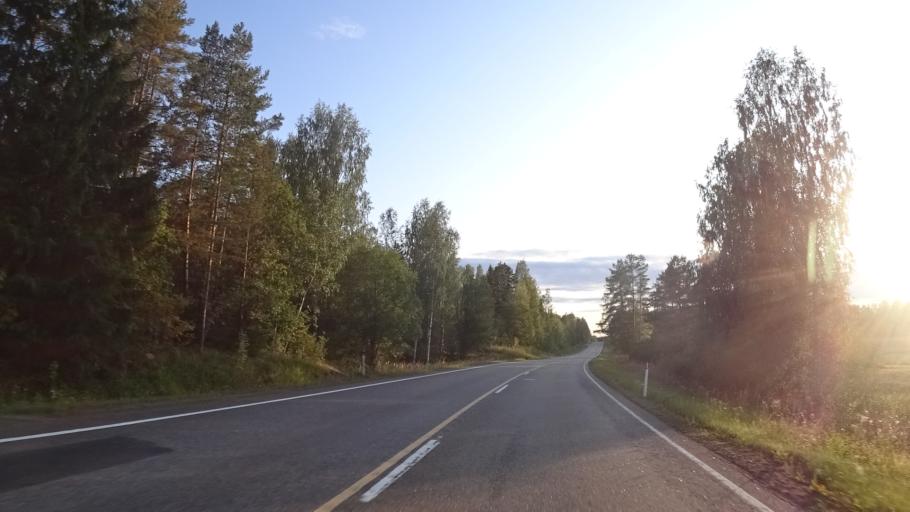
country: FI
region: South Karelia
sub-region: Lappeenranta
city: Ylaemaa
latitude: 60.7259
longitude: 27.9927
